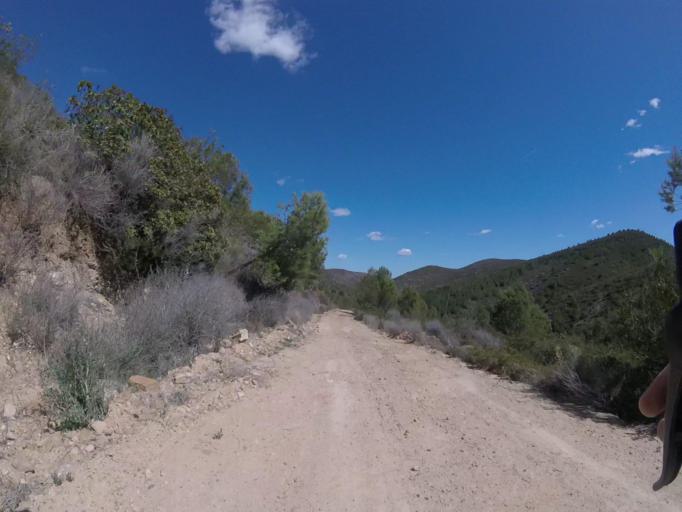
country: ES
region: Valencia
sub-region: Provincia de Castello
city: Cabanes
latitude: 40.1582
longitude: 0.1046
